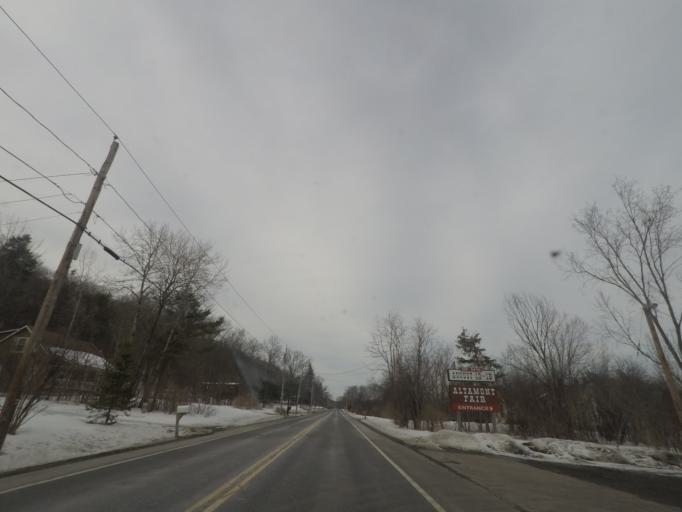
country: US
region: New York
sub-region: Albany County
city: Altamont
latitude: 42.6934
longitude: -74.0275
